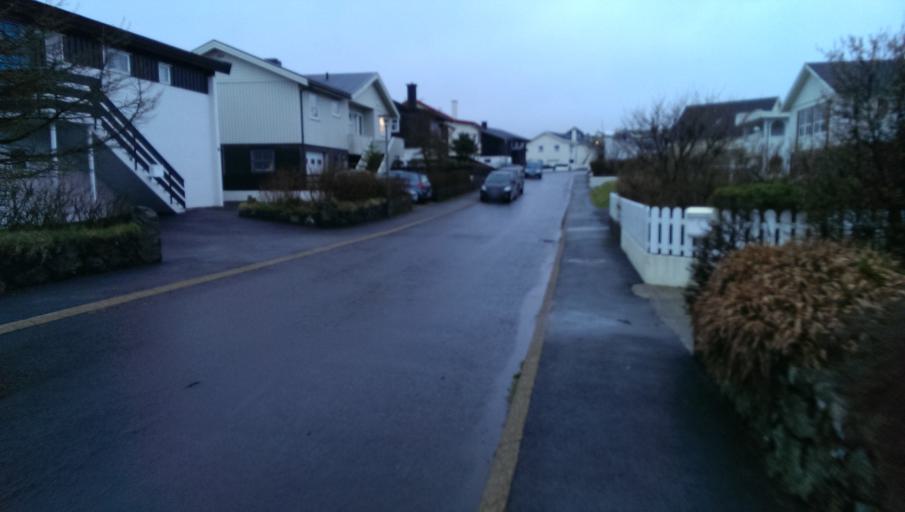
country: FO
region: Streymoy
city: Hoyvik
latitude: 62.0320
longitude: -6.7875
